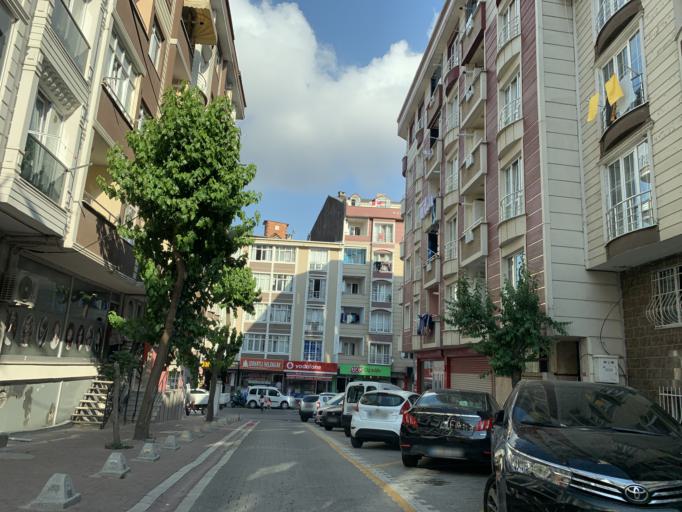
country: TR
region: Istanbul
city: Esenyurt
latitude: 41.0441
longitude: 28.6777
